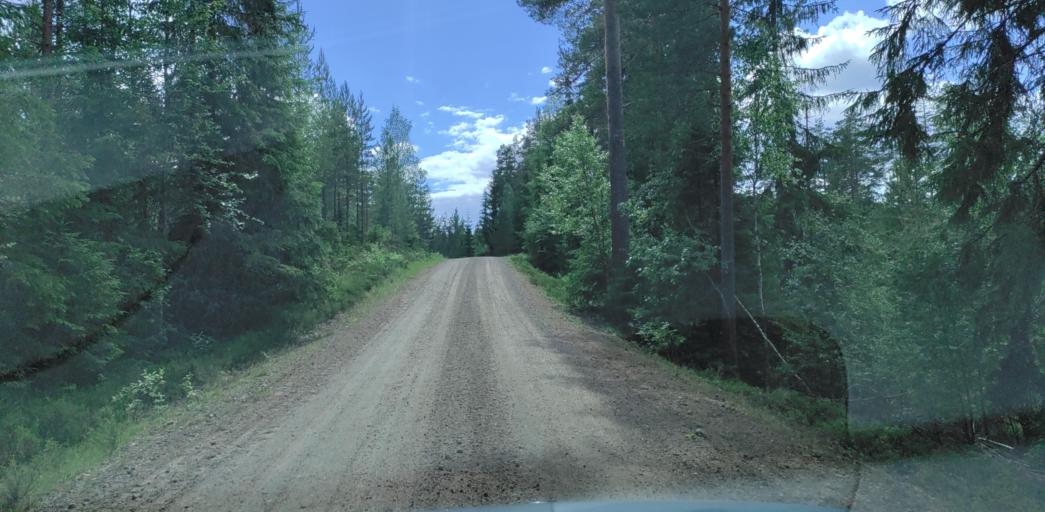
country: SE
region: Vaermland
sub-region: Hagfors Kommun
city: Ekshaerad
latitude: 60.0789
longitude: 13.2922
